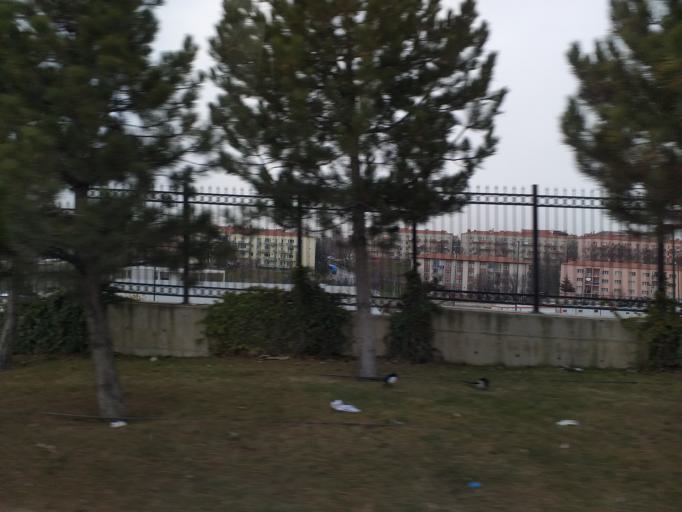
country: TR
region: Ankara
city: Ankara
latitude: 39.9615
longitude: 32.8219
